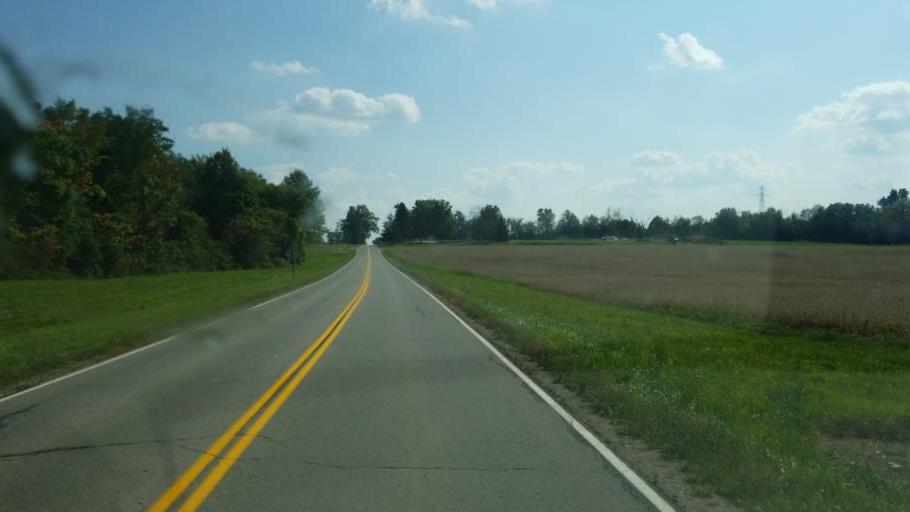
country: US
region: Ohio
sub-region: Richland County
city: Ontario
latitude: 40.7819
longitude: -82.6294
